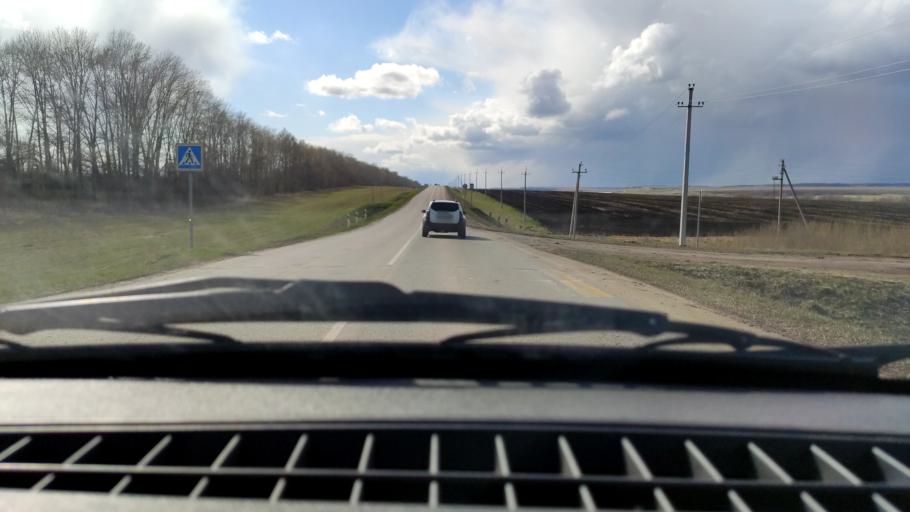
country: RU
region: Bashkortostan
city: Chekmagush
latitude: 55.1122
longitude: 54.9020
